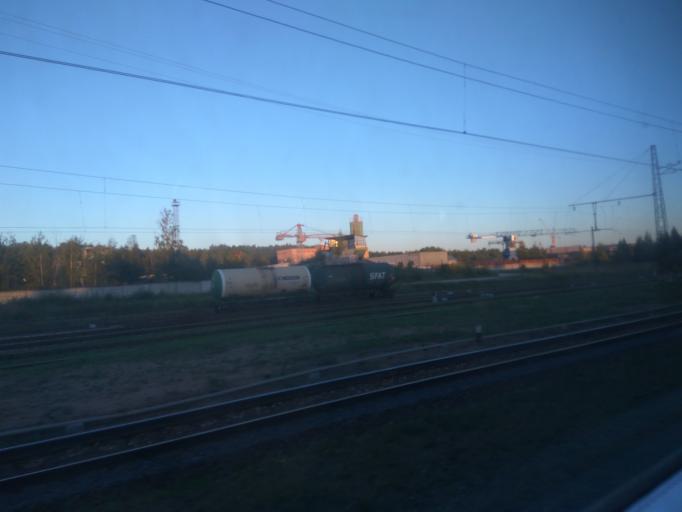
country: RU
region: Moskovskaya
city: Elektrostal'
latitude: 55.7678
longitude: 38.4691
